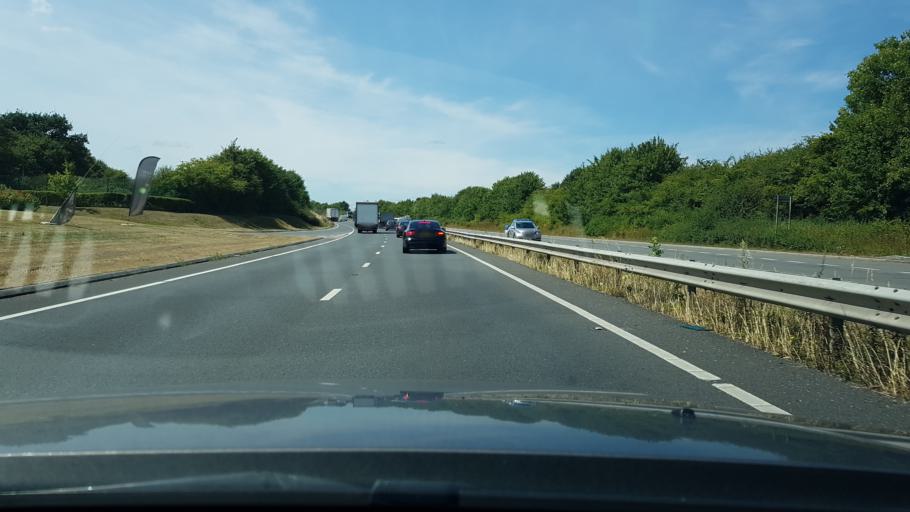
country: GB
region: England
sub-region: Hampshire
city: Emsworth
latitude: 50.8531
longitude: -0.9449
